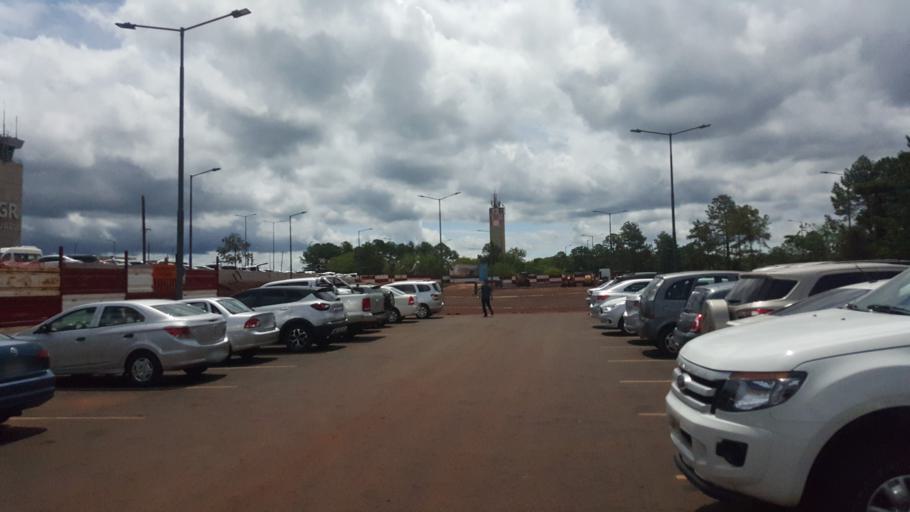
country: AR
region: Misiones
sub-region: Departamento de Iguazu
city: Puerto Iguazu
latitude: -25.7310
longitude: -54.4759
